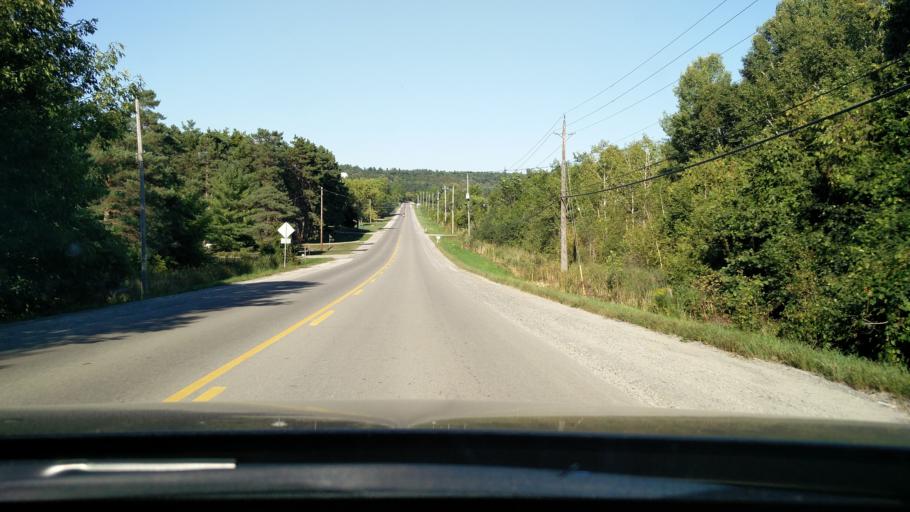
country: CA
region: Ontario
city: Perth
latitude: 44.6746
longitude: -76.4180
